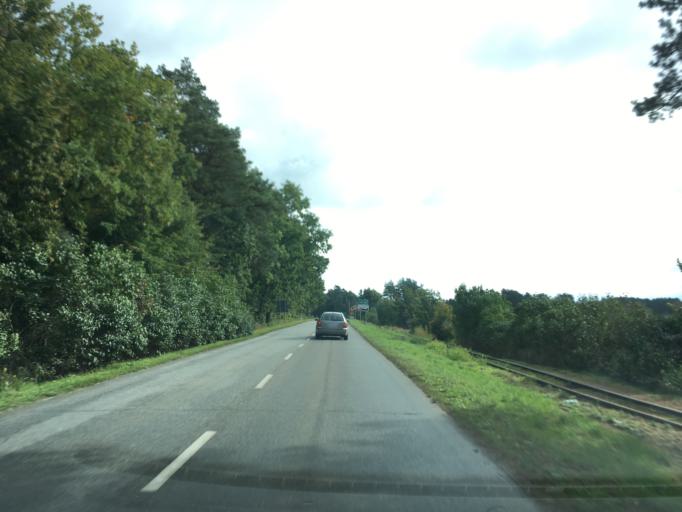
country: PL
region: Pomeranian Voivodeship
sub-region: Powiat nowodworski
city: Stegna
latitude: 54.3330
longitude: 19.0524
